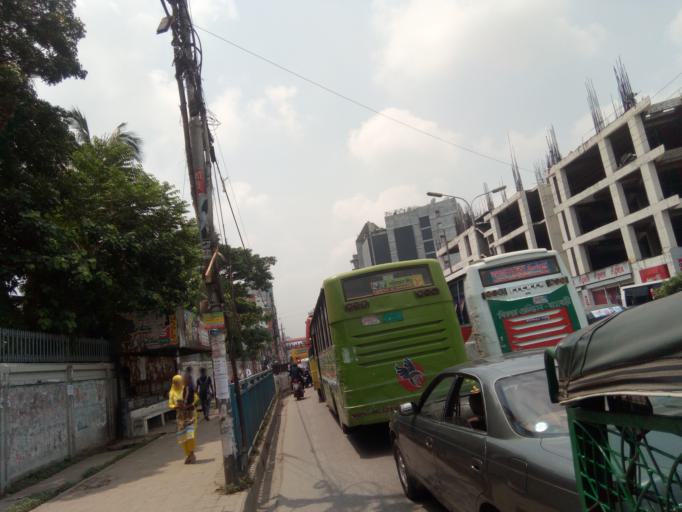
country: BD
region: Dhaka
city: Azimpur
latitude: 23.7573
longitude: 90.3905
